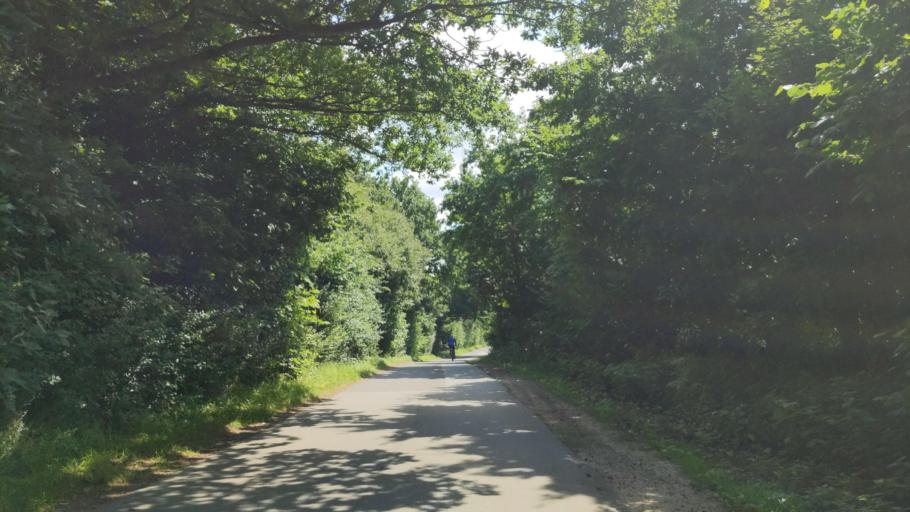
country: DE
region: Schleswig-Holstein
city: Scharbeutz
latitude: 54.0074
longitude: 10.7055
